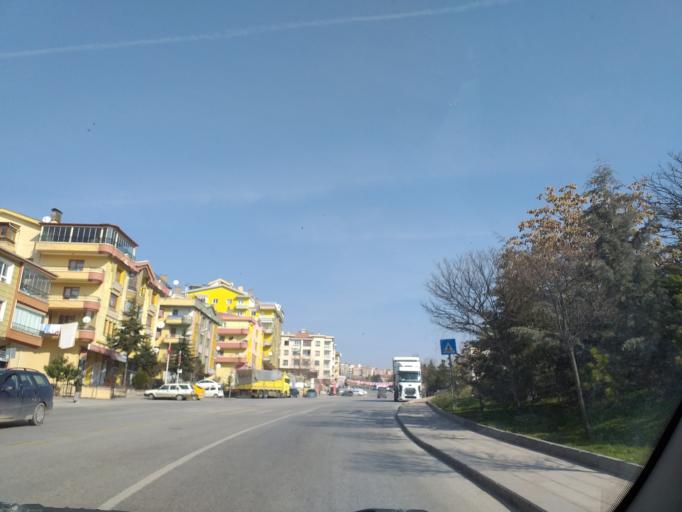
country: TR
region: Ankara
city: Ankara
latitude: 39.9961
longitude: 32.8545
